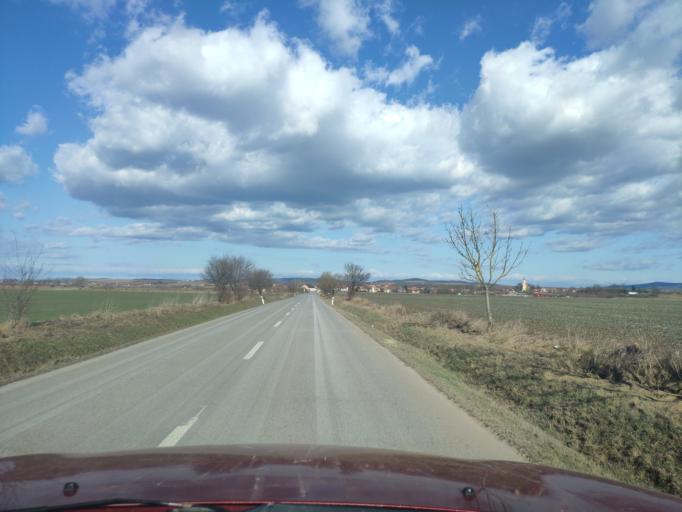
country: HU
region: Borsod-Abauj-Zemplen
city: Ozd
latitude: 48.3126
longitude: 20.3249
